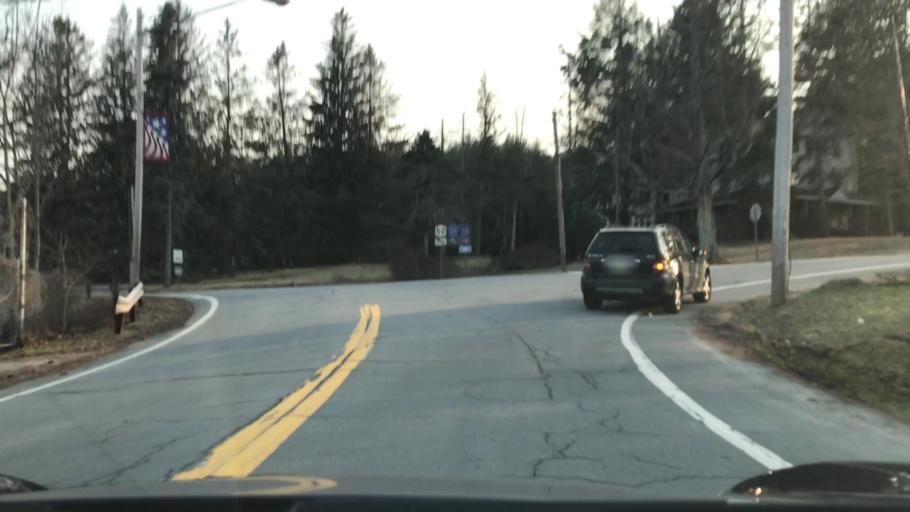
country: US
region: New York
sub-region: Sullivan County
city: Livingston Manor
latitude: 41.6822
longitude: -74.9939
